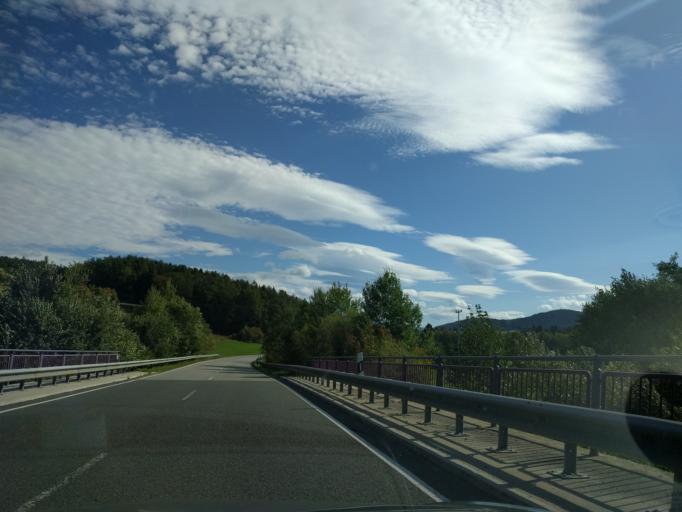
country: DE
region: Bavaria
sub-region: Upper Palatinate
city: Grafenwiesen
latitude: 49.2102
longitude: 12.8929
